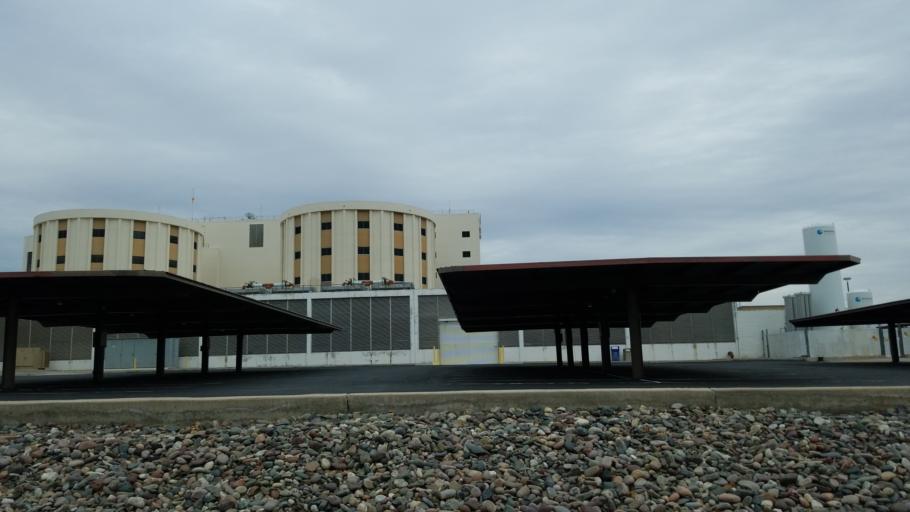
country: US
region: Arizona
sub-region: Maricopa County
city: Sun City
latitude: 33.6035
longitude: -112.2852
